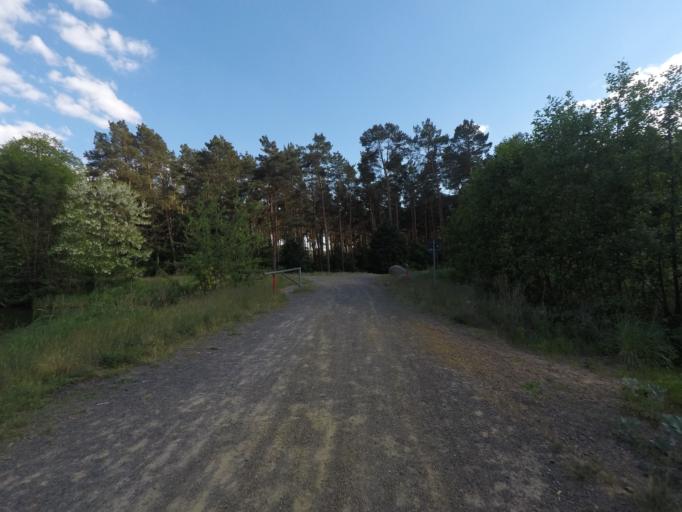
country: DE
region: Brandenburg
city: Eberswalde
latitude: 52.8541
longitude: 13.8123
